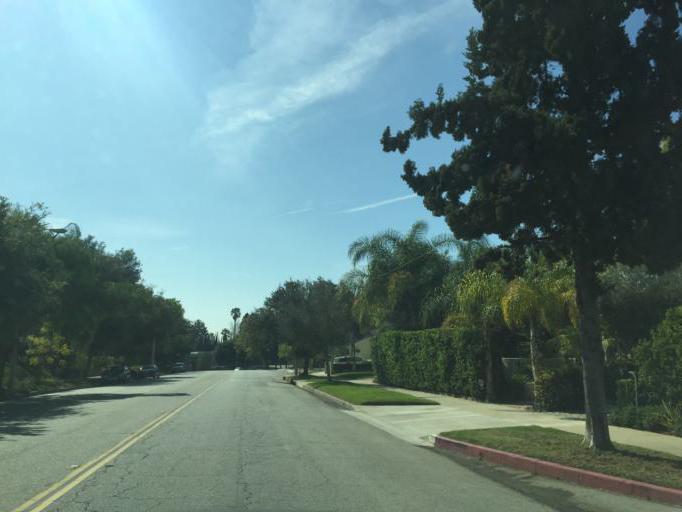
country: US
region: California
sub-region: Los Angeles County
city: Pasadena
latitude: 34.1327
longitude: -118.1323
